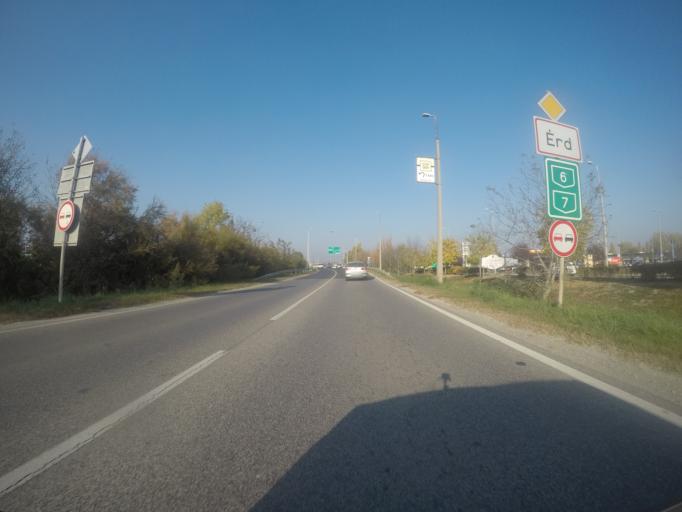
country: HU
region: Pest
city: Erd
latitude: 47.3770
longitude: 18.9354
